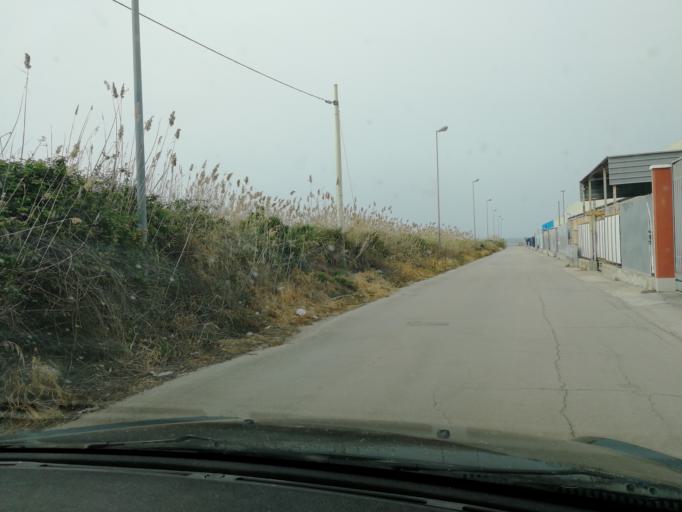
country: IT
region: Apulia
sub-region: Provincia di Barletta - Andria - Trani
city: Barletta
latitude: 41.3133
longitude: 16.3104
